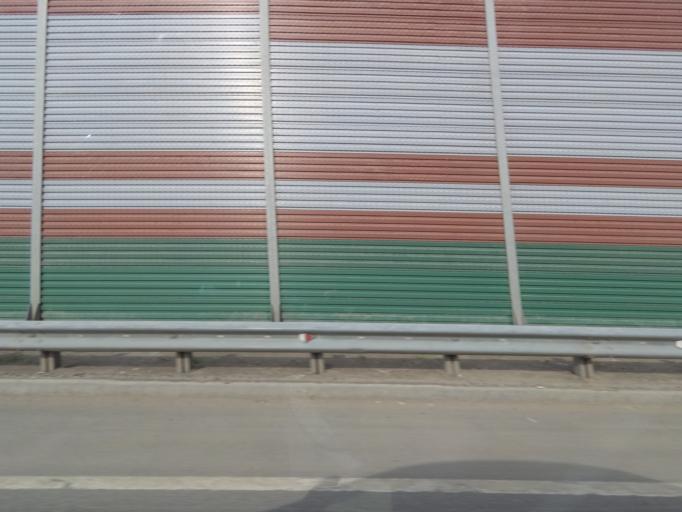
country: RU
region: Moscow
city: Businovo
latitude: 55.8982
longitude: 37.4920
